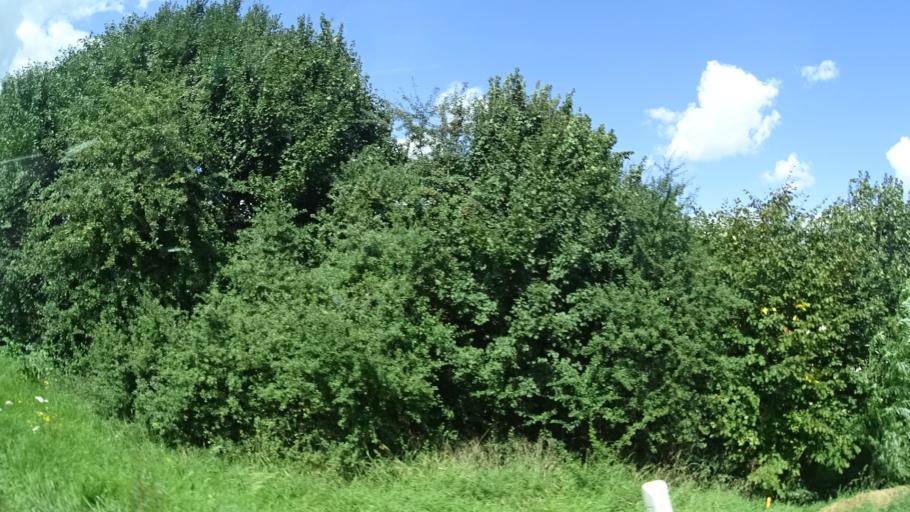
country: DE
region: Bavaria
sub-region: Regierungsbezirk Unterfranken
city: Sand
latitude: 49.9840
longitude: 10.6252
